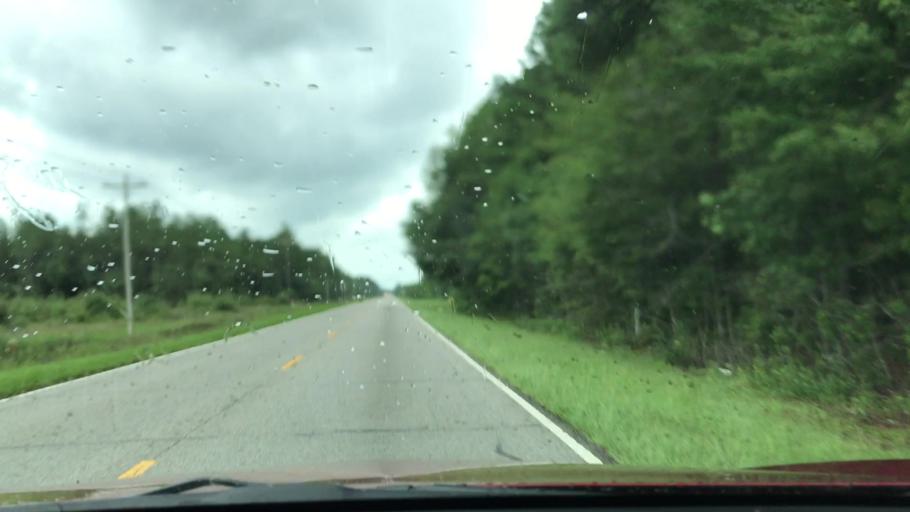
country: US
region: South Carolina
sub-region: Georgetown County
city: Georgetown
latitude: 33.5209
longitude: -79.2457
